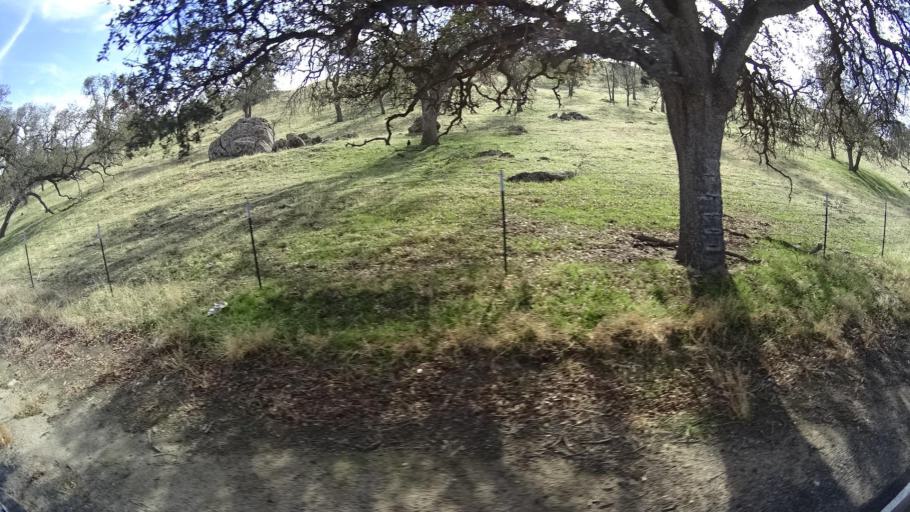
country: US
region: California
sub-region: Kern County
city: Oildale
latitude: 35.6230
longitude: -118.8453
